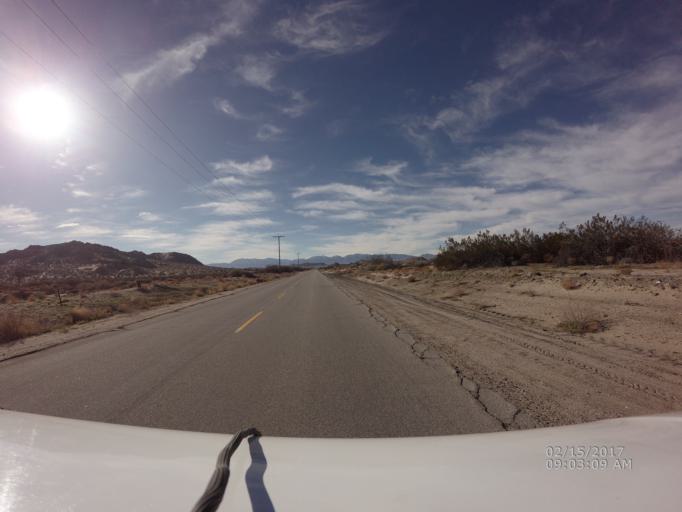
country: US
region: California
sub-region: Los Angeles County
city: Lake Los Angeles
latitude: 34.6689
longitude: -117.8631
